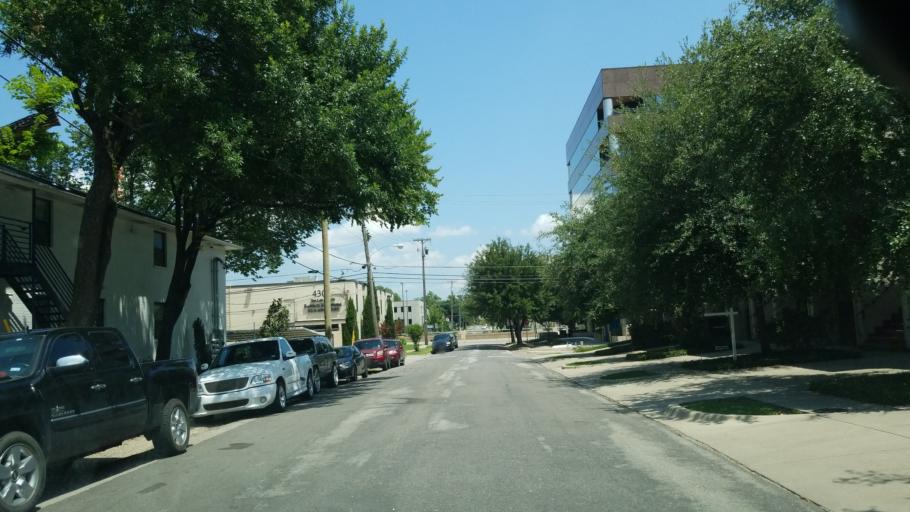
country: US
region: Texas
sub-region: Dallas County
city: Highland Park
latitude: 32.8177
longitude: -96.7899
